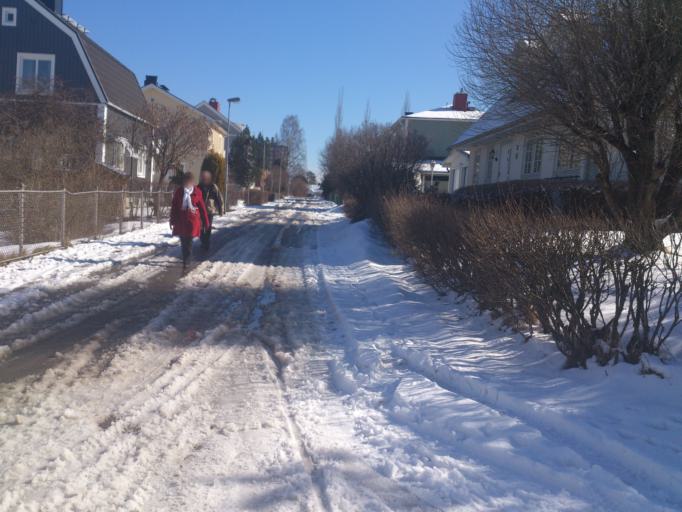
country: SE
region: Vaesternorrland
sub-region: Sundsvalls Kommun
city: Sundsvall
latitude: 62.3801
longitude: 17.3270
